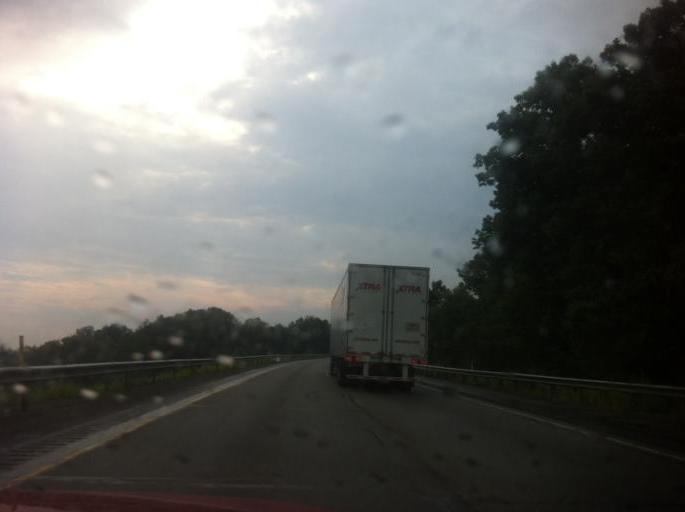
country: US
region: Pennsylvania
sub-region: Clarion County
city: Clarion
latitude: 41.1779
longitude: -79.3721
